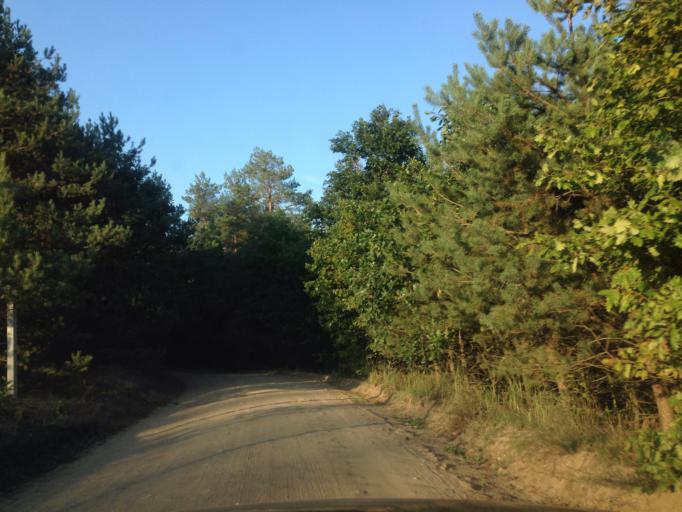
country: PL
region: Kujawsko-Pomorskie
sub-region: Powiat brodnicki
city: Gorzno
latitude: 53.2746
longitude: 19.7062
